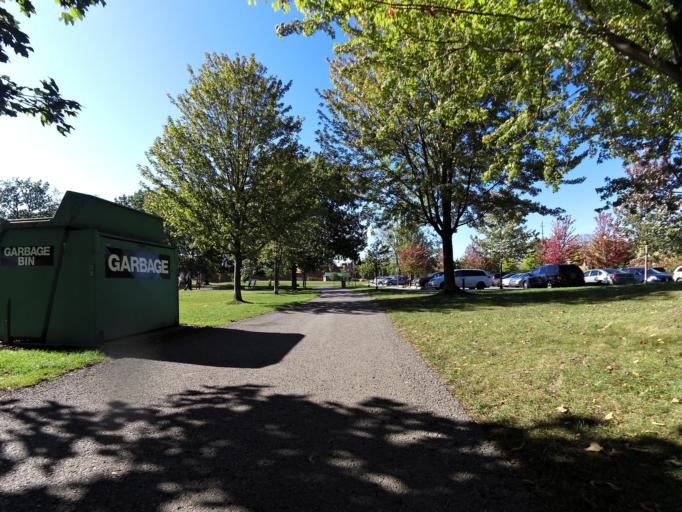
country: CA
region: Ontario
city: Oshawa
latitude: 43.8511
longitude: -78.9217
